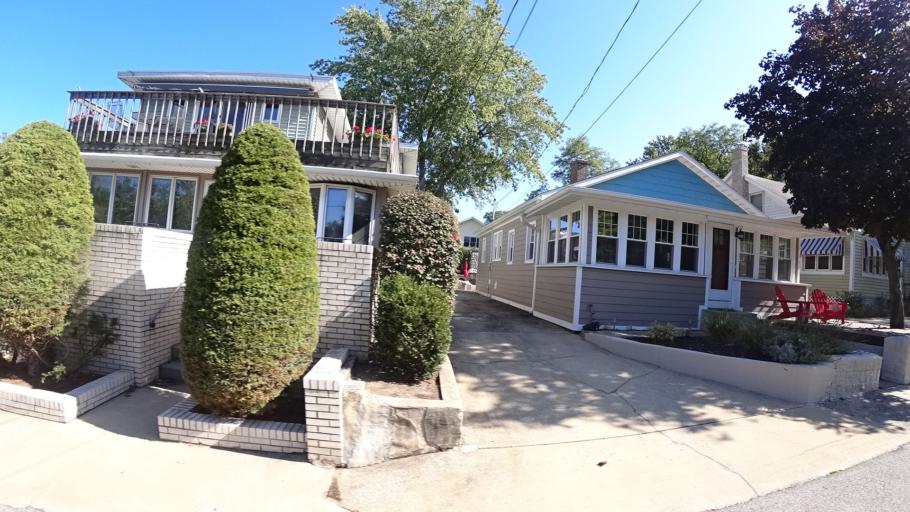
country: US
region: Indiana
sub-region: LaPorte County
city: Michigan City
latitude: 41.7307
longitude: -86.8891
